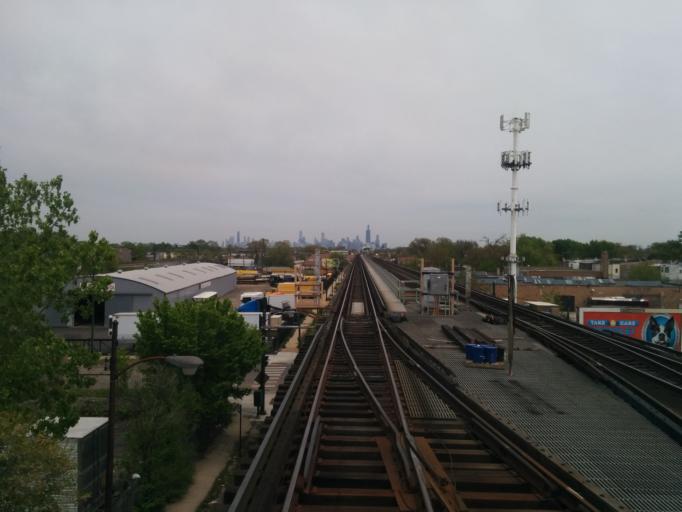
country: US
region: Illinois
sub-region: Cook County
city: Oak Park
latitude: 41.8870
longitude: -87.7507
